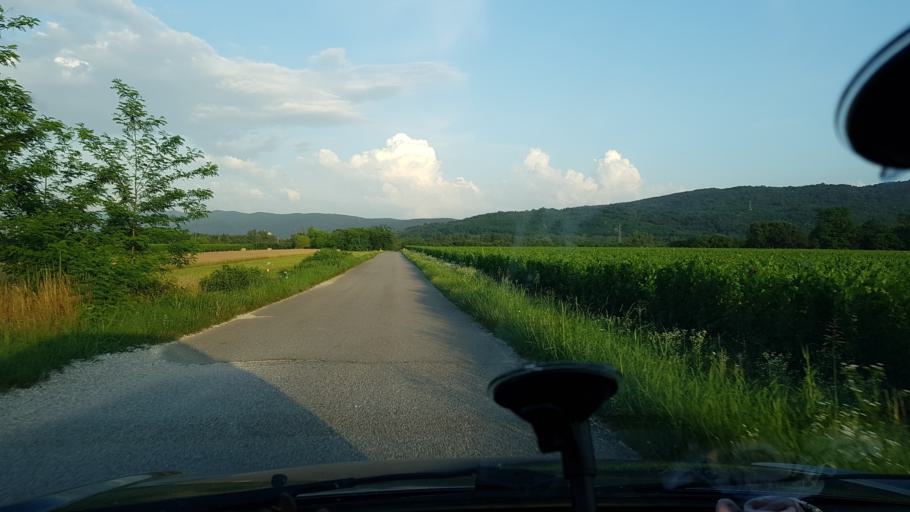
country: IT
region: Friuli Venezia Giulia
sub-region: Provincia di Gorizia
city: Mossa
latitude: 45.9112
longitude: 13.5484
